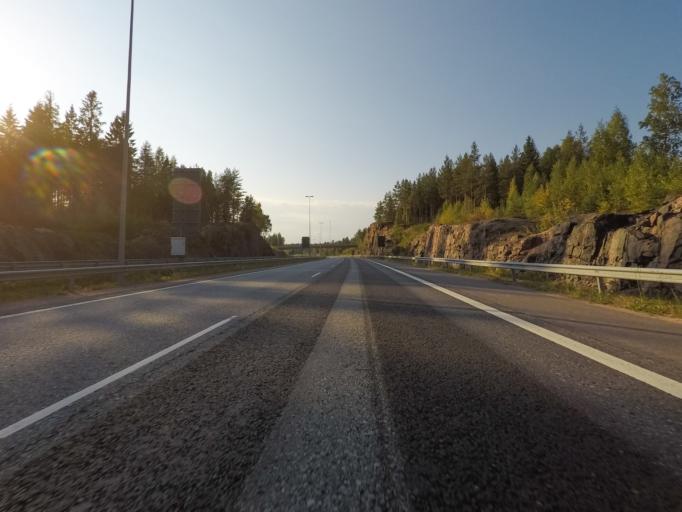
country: FI
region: Uusimaa
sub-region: Helsinki
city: Saukkola
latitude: 60.3198
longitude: 23.9659
